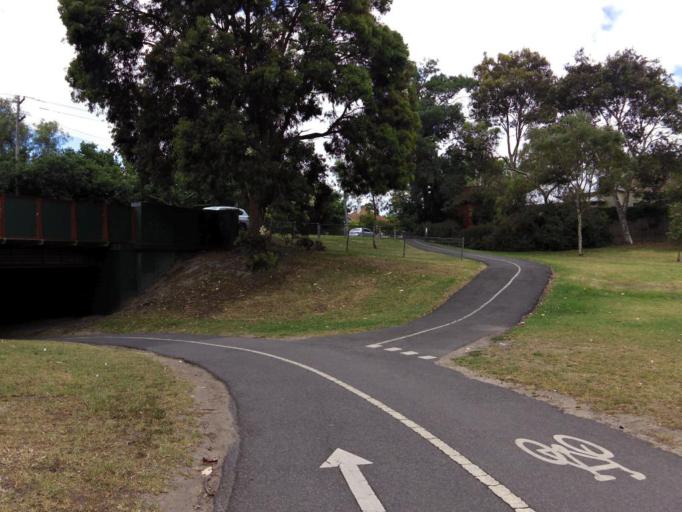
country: AU
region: Victoria
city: Balwyn
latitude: -37.8217
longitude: 145.0675
